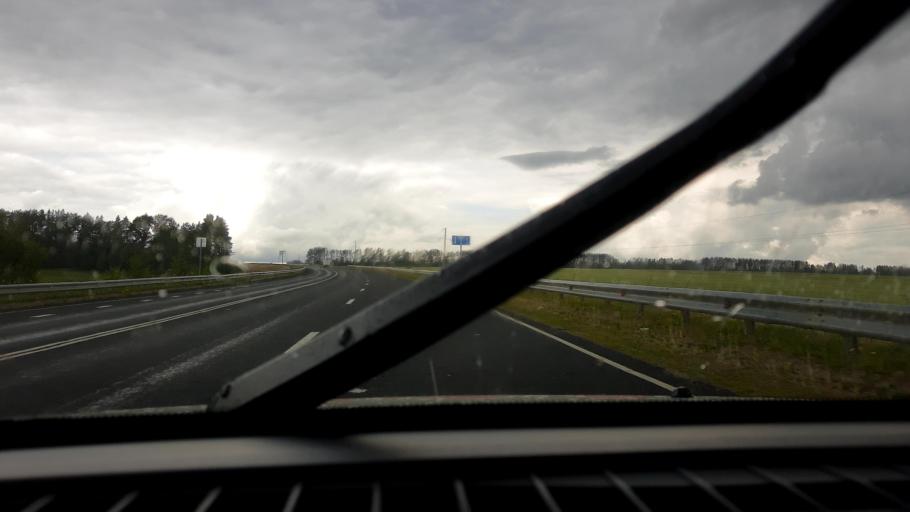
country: RU
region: Nizjnij Novgorod
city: Bol'shoye Murashkino
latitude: 55.8897
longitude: 44.7436
